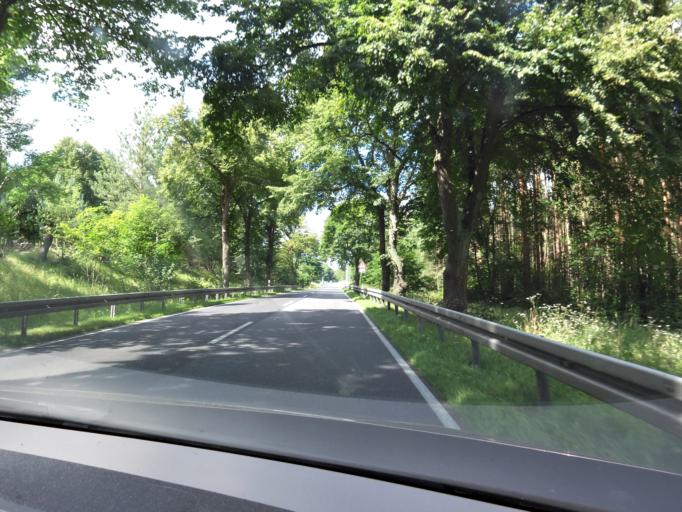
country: DE
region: Brandenburg
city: Furstenberg
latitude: 53.1538
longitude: 13.1491
